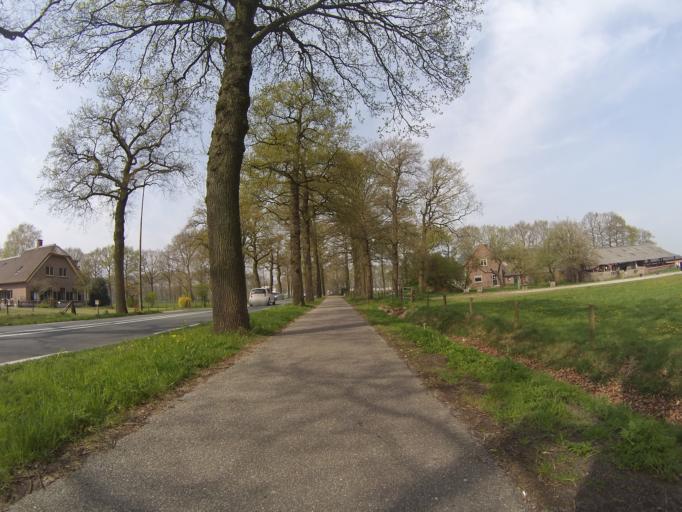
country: NL
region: Utrecht
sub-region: Gemeente Soest
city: Soest
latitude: 52.1612
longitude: 5.3247
